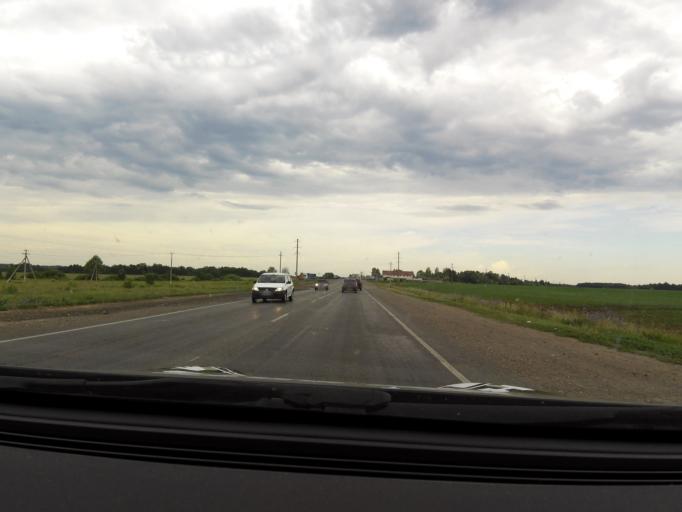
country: RU
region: Bashkortostan
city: Kudeyevskiy
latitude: 54.8169
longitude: 56.7429
